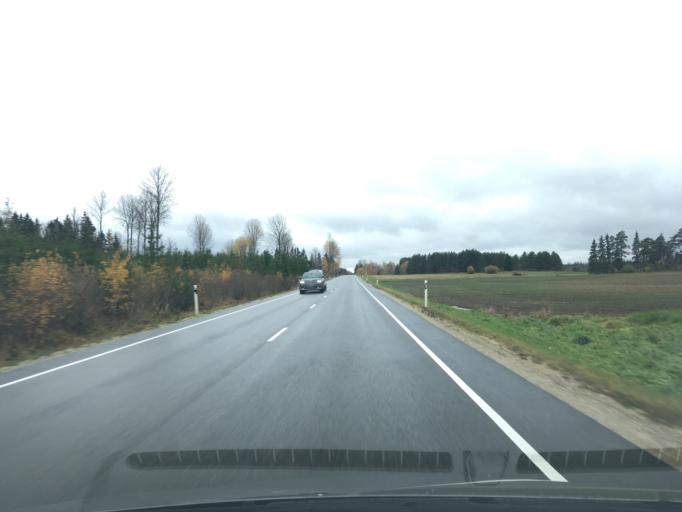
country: EE
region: Jogevamaa
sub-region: Tabivere vald
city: Tabivere
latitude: 58.4490
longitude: 26.5182
